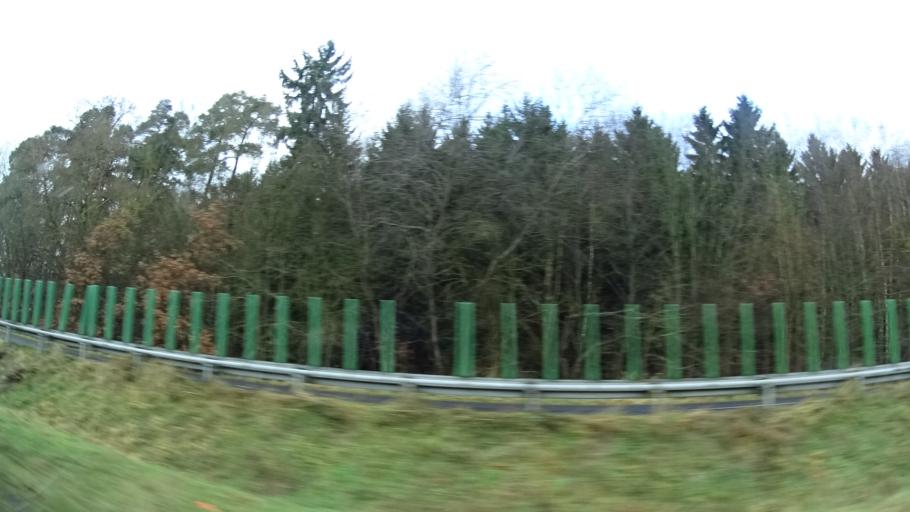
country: DE
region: Hesse
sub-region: Regierungsbezirk Kassel
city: Flieden
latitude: 50.4085
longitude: 9.5581
